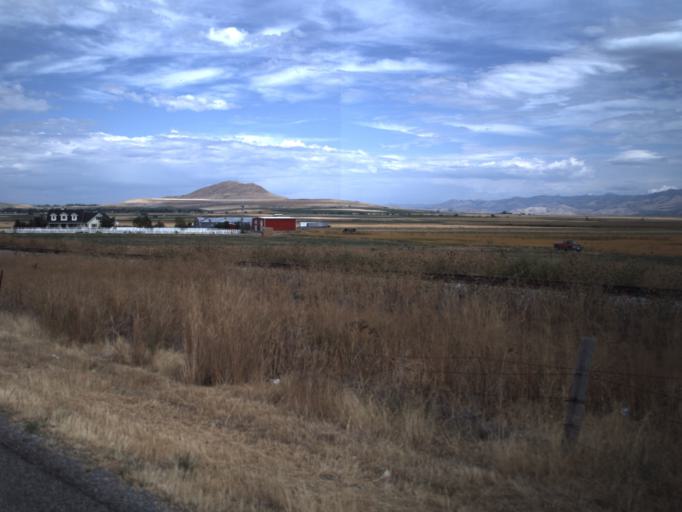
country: US
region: Utah
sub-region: Cache County
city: Benson
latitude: 41.8128
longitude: -111.9958
